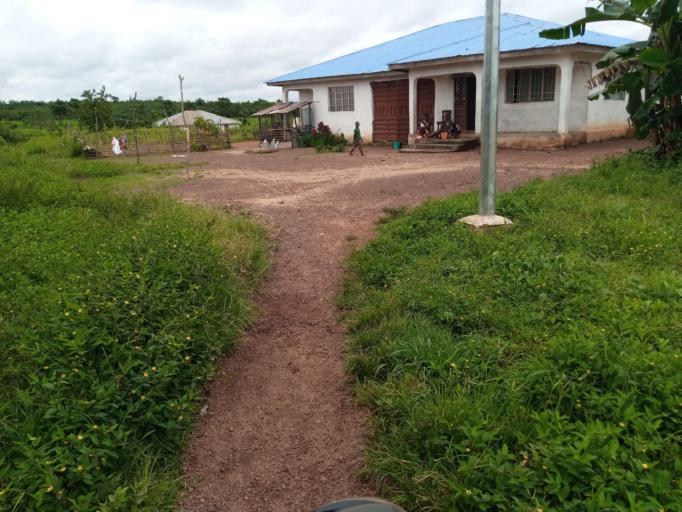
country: SL
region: Southern Province
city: Largo
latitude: 8.1917
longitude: -12.0606
